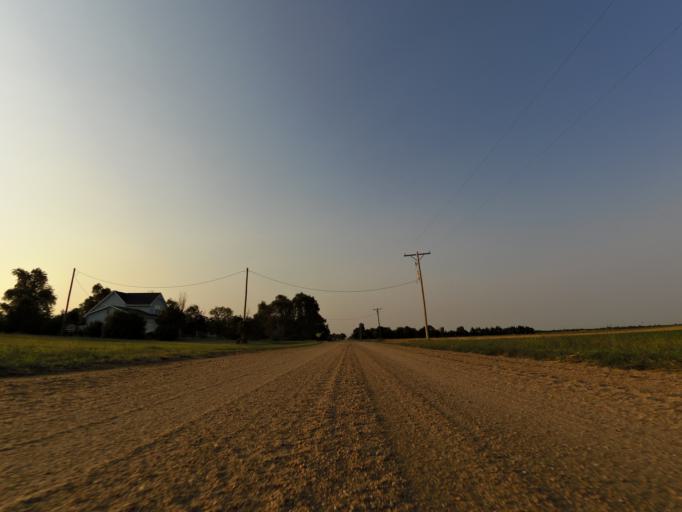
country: US
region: Kansas
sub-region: Reno County
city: South Hutchinson
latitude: 38.0048
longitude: -97.9954
